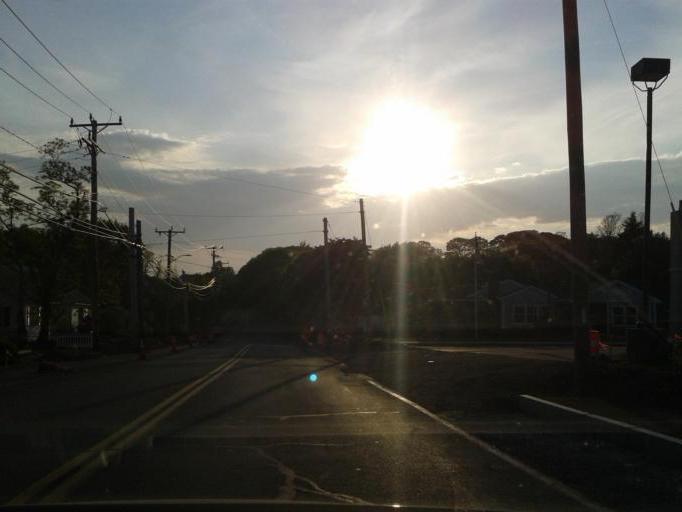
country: US
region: Massachusetts
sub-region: Barnstable County
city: Teaticket
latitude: 41.5611
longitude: -70.5994
